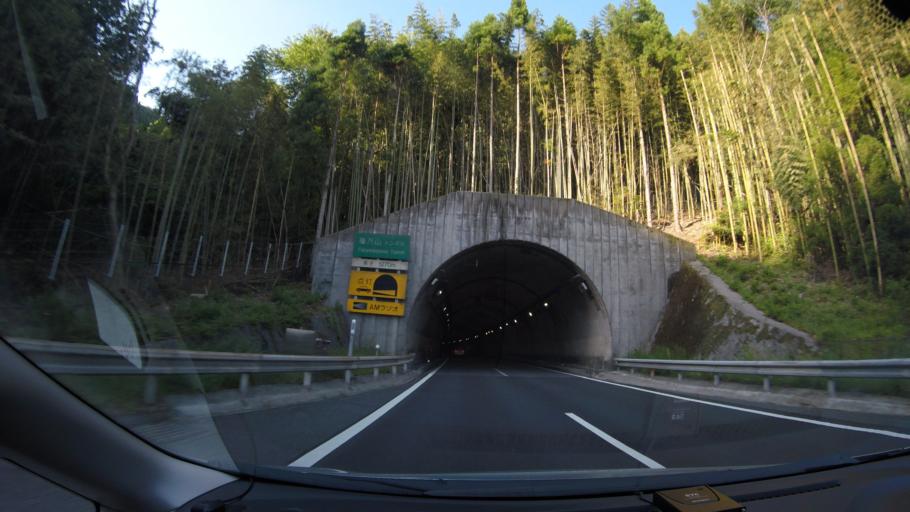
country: JP
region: Oita
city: Beppu
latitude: 33.2684
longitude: 131.3399
